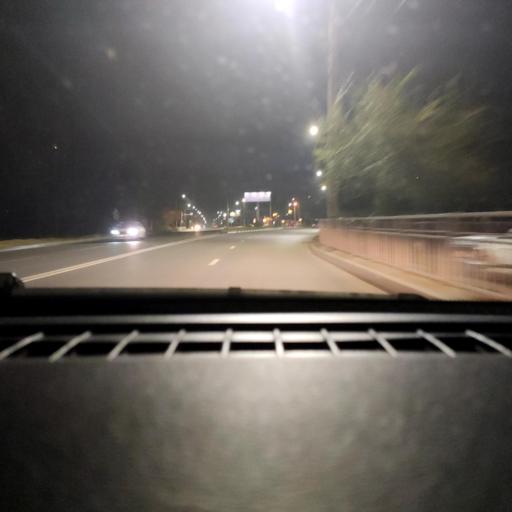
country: RU
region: Voronezj
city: Podgornoye
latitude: 51.7011
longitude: 39.1450
